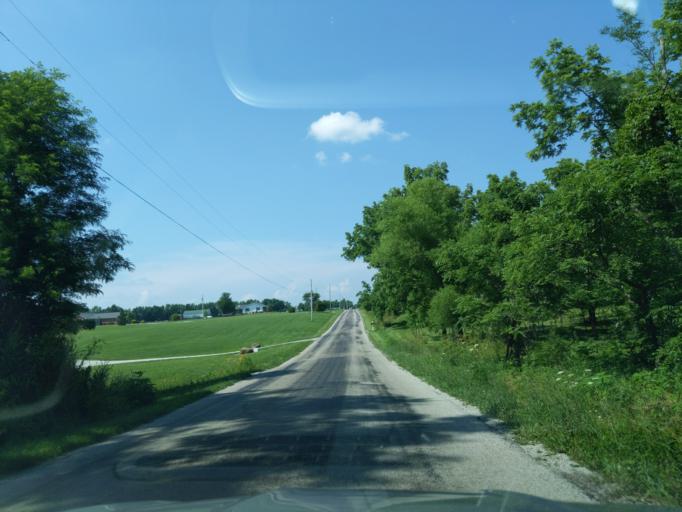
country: US
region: Indiana
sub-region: Ripley County
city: Osgood
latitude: 39.0830
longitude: -85.3476
